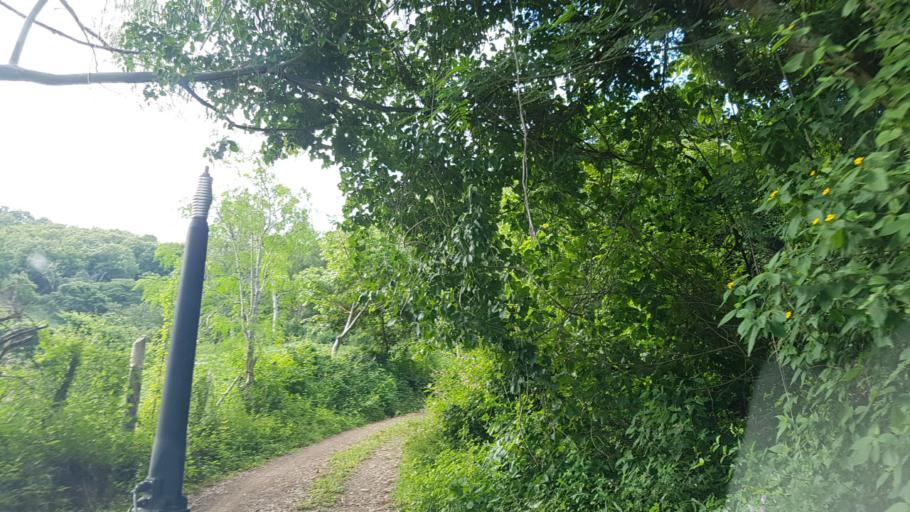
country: NI
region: Nueva Segovia
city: Ciudad Antigua
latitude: 13.6263
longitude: -86.2842
